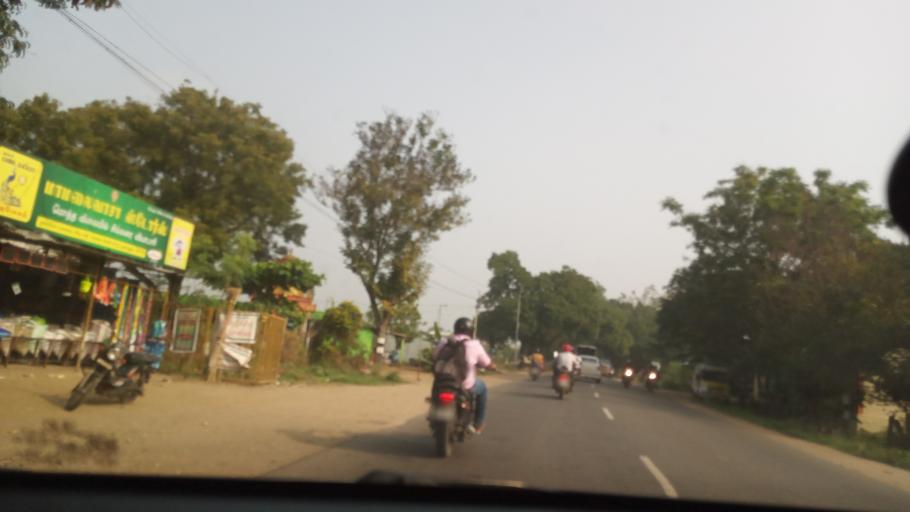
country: IN
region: Tamil Nadu
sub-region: Coimbatore
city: Annur
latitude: 11.1562
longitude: 77.0500
